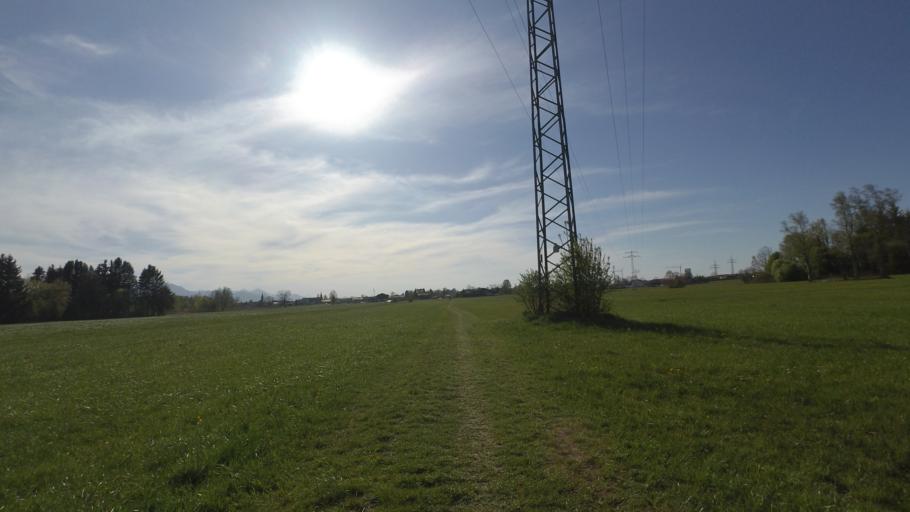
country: DE
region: Bavaria
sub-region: Upper Bavaria
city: Grabenstatt
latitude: 47.8467
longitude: 12.5547
